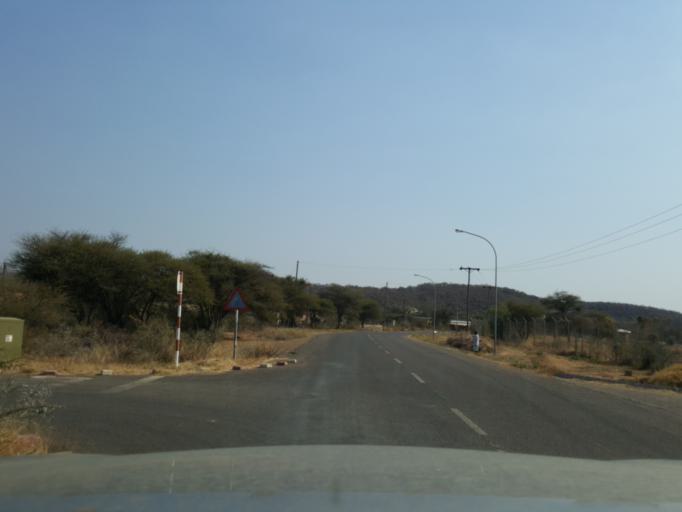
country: BW
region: South East
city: Lobatse
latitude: -25.1878
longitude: 25.6943
